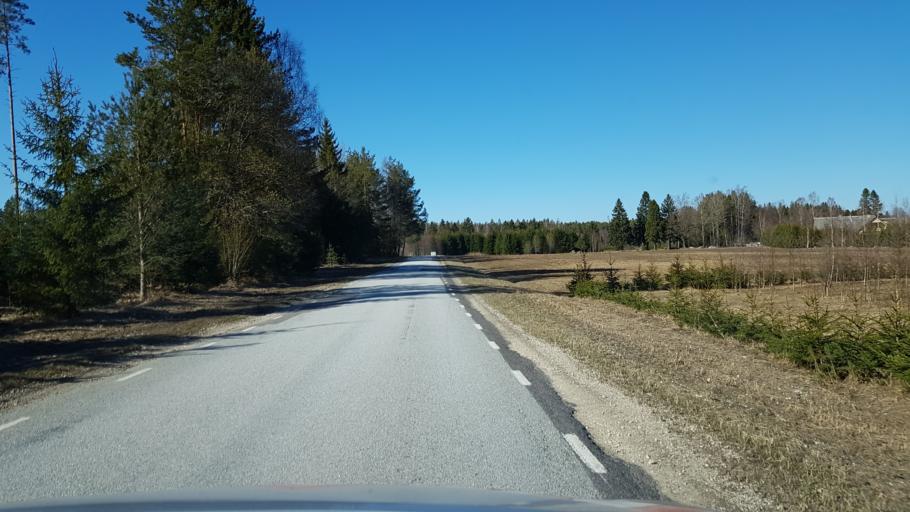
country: EE
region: Laeaene-Virumaa
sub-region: Viru-Nigula vald
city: Kunda
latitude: 59.3757
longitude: 26.5783
